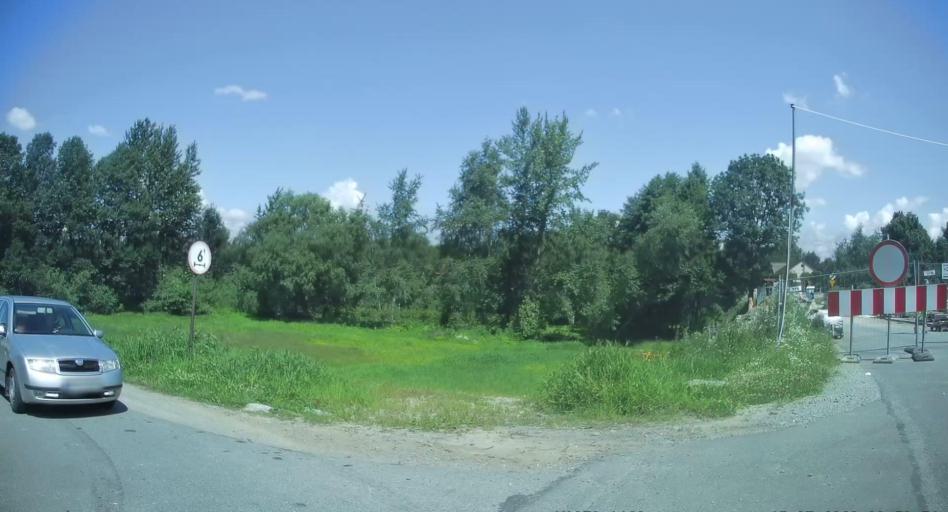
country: PL
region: Subcarpathian Voivodeship
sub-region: Powiat jaroslawski
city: Sosnica
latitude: 49.8623
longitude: 22.8817
